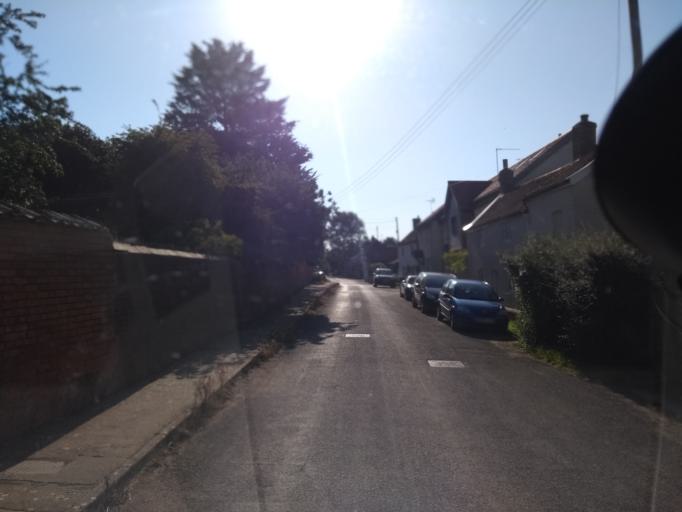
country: GB
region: England
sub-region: Somerset
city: Westonzoyland
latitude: 51.1404
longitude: -2.9060
